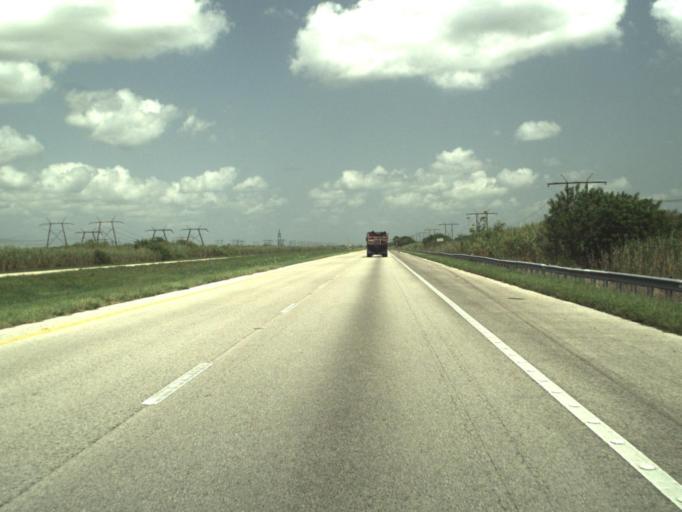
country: US
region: Florida
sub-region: Broward County
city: Weston
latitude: 26.2882
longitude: -80.5016
